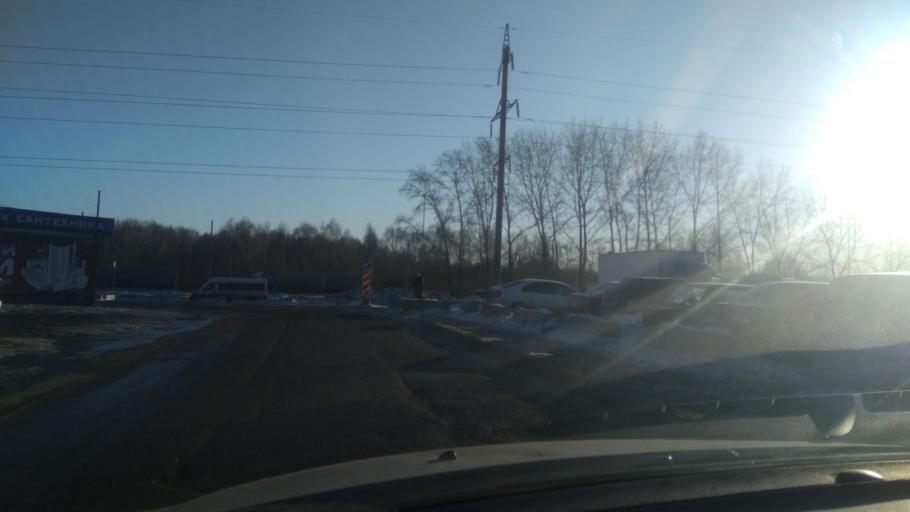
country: RU
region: Sverdlovsk
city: Istok
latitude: 56.8245
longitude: 60.6989
